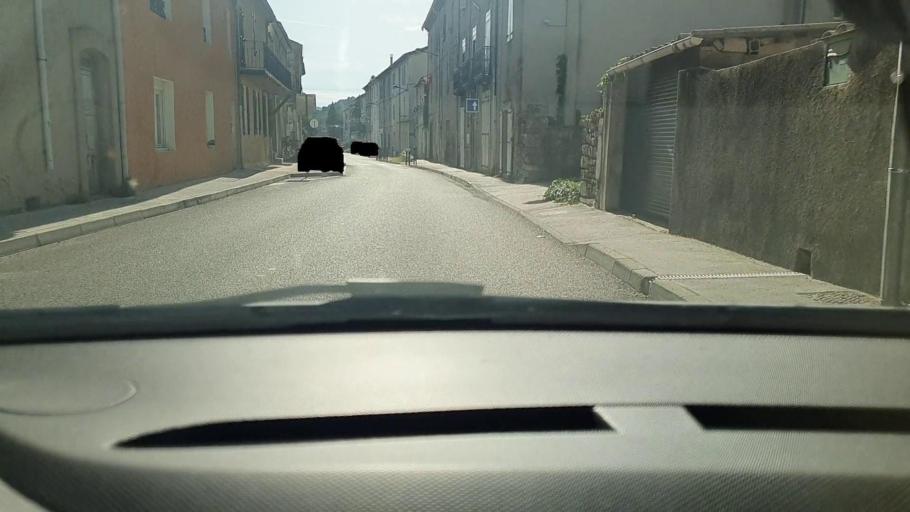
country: FR
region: Languedoc-Roussillon
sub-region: Departement du Gard
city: Saint-Florent-sur-Auzonnet
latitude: 44.2521
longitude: 4.0859
